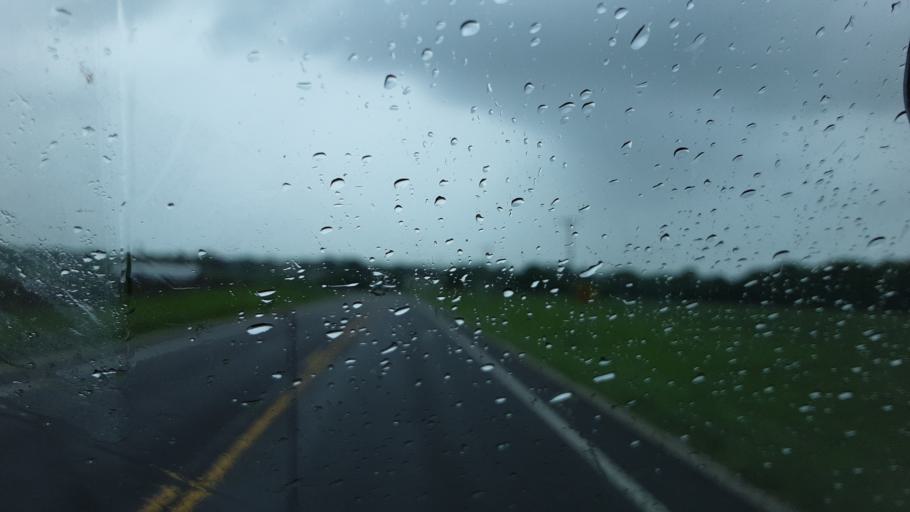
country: US
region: Missouri
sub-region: Monroe County
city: Paris
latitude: 39.4768
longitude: -92.1944
